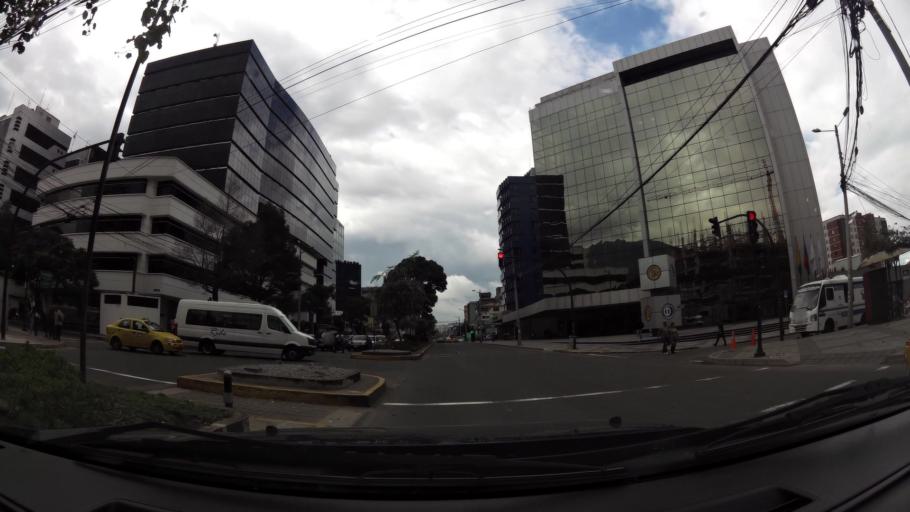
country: EC
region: Pichincha
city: Quito
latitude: -0.1718
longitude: -78.4848
